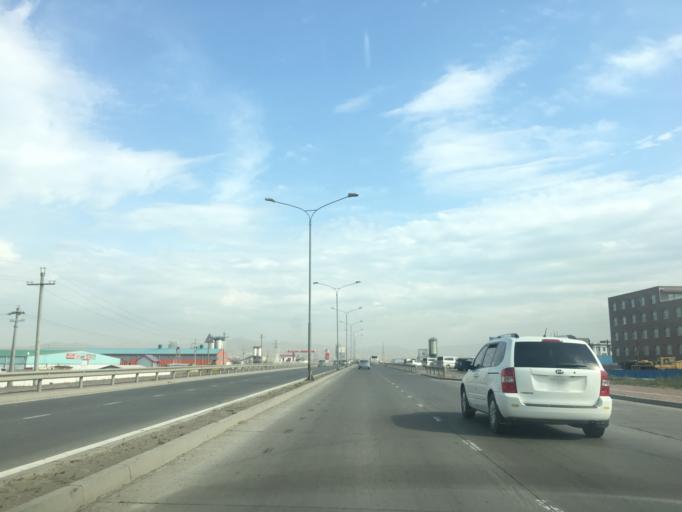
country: MN
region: Ulaanbaatar
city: Ulaanbaatar
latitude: 47.8799
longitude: 106.7845
